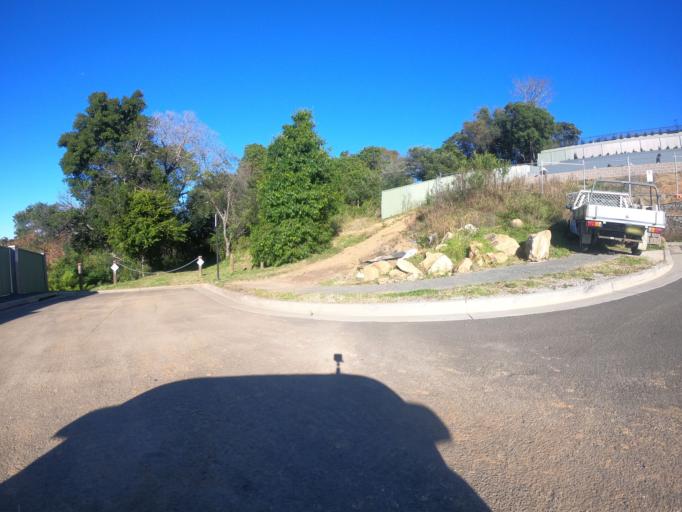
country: AU
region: New South Wales
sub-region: Wollongong
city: Cordeaux Heights
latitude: -34.4411
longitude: 150.8441
